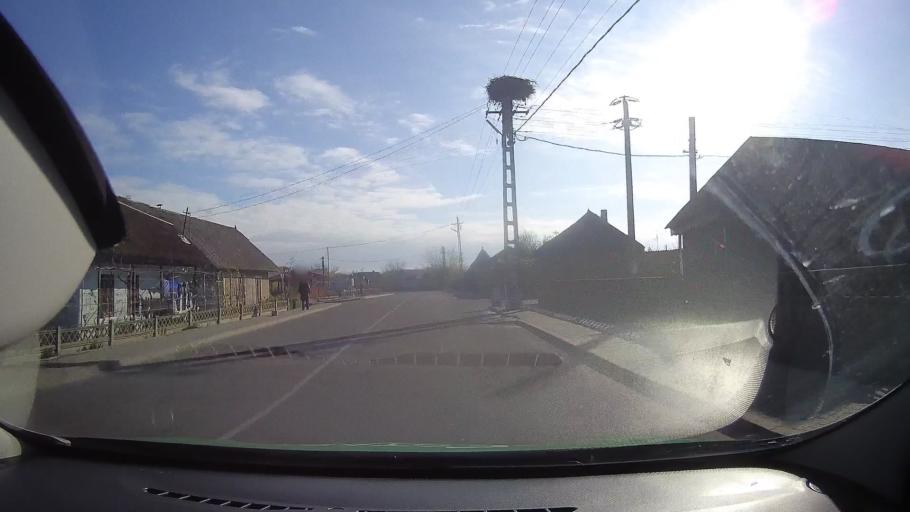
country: RO
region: Tulcea
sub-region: Comuna Murighiol
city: Murighiol
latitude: 45.0377
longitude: 29.1613
